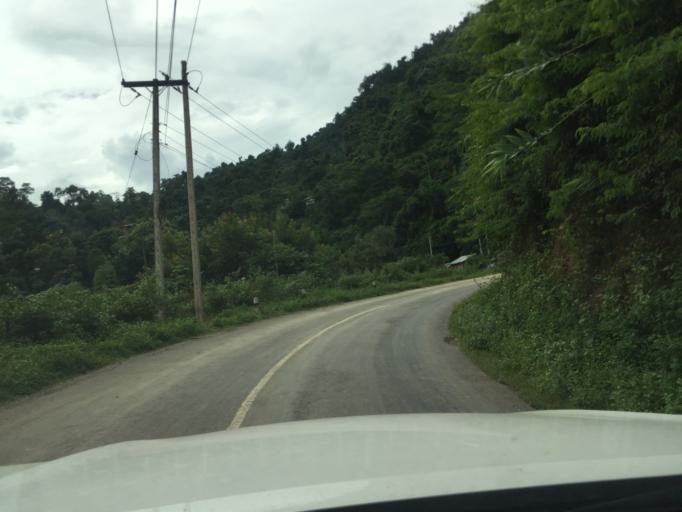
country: LA
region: Oudomxai
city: Muang La
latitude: 21.1103
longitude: 102.2093
